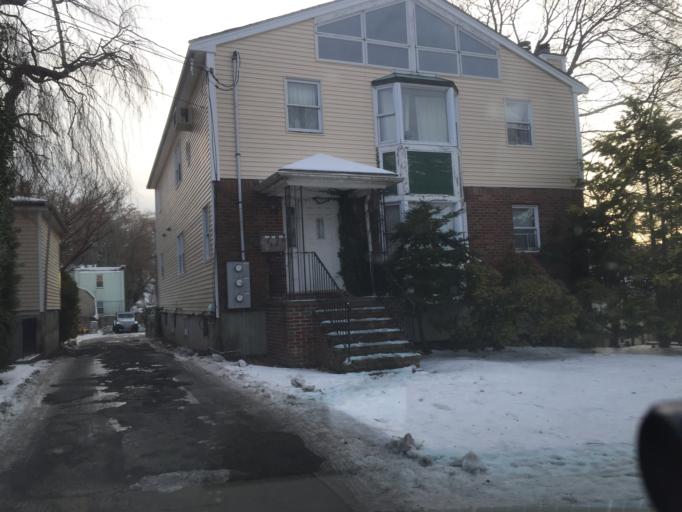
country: US
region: Massachusetts
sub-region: Middlesex County
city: Watertown
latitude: 42.3480
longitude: -71.1560
